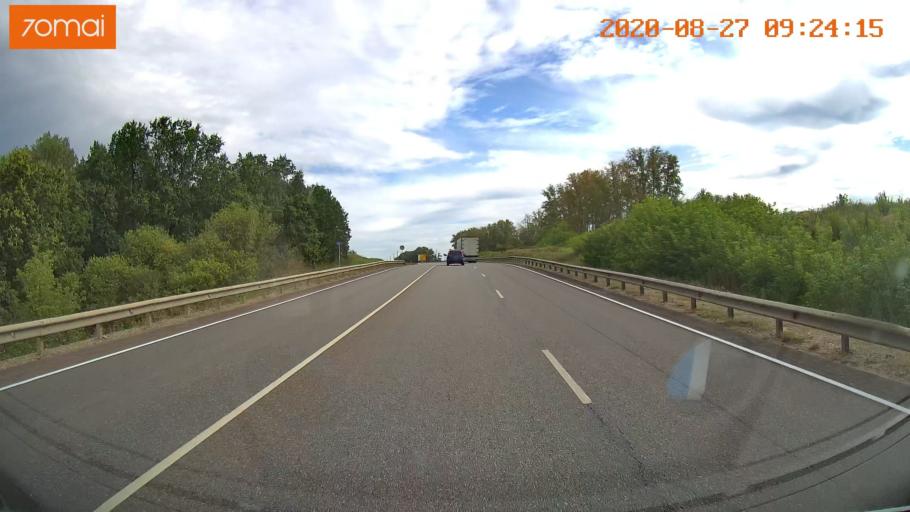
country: RU
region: Tula
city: Kazachka
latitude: 53.2846
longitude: 38.1745
